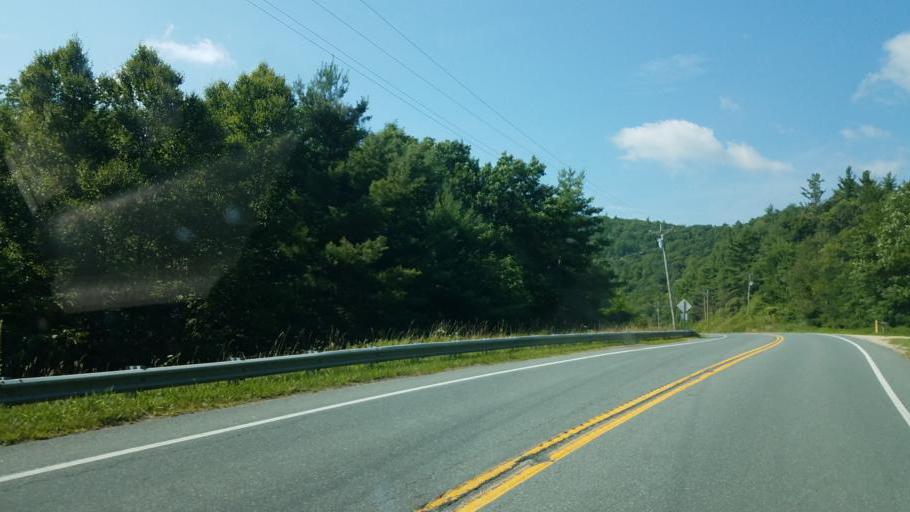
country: US
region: North Carolina
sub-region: Avery County
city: Newland
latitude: 35.9726
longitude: -81.8949
